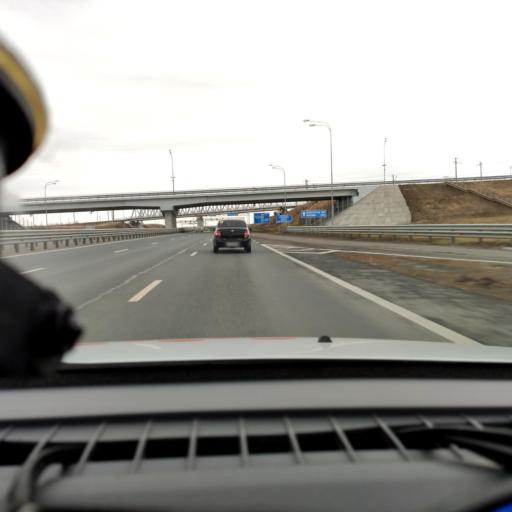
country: RU
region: Samara
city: Smyshlyayevka
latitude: 53.1489
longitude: 50.3809
